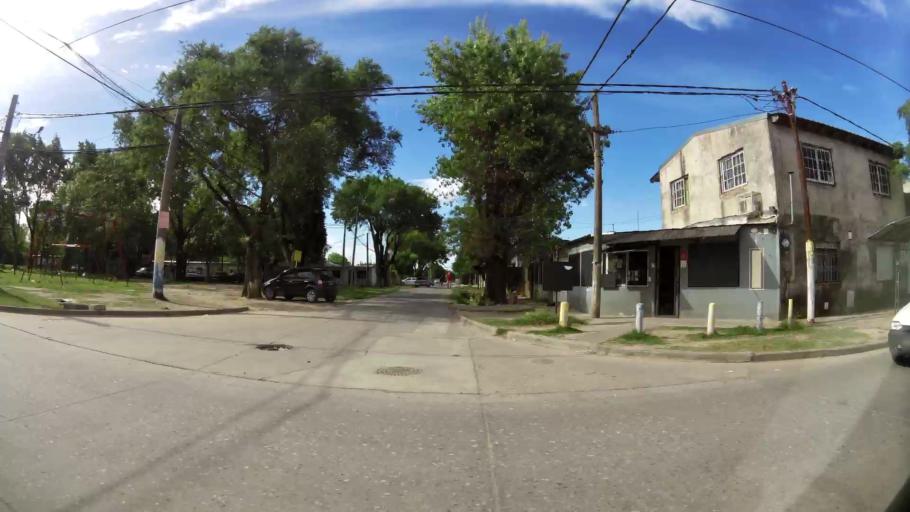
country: AR
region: Santa Fe
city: Granadero Baigorria
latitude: -32.9151
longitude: -60.7194
